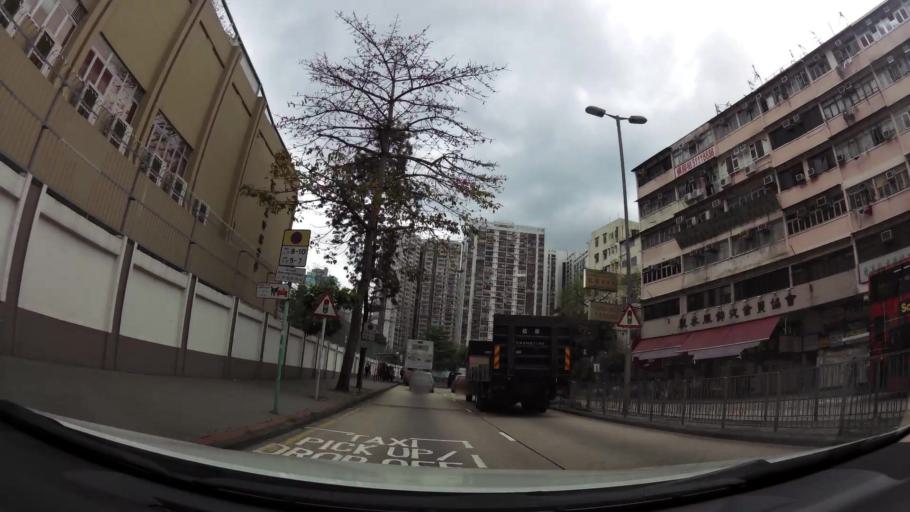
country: HK
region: Wong Tai Sin
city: Wong Tai Sin
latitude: 22.3341
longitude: 114.1945
